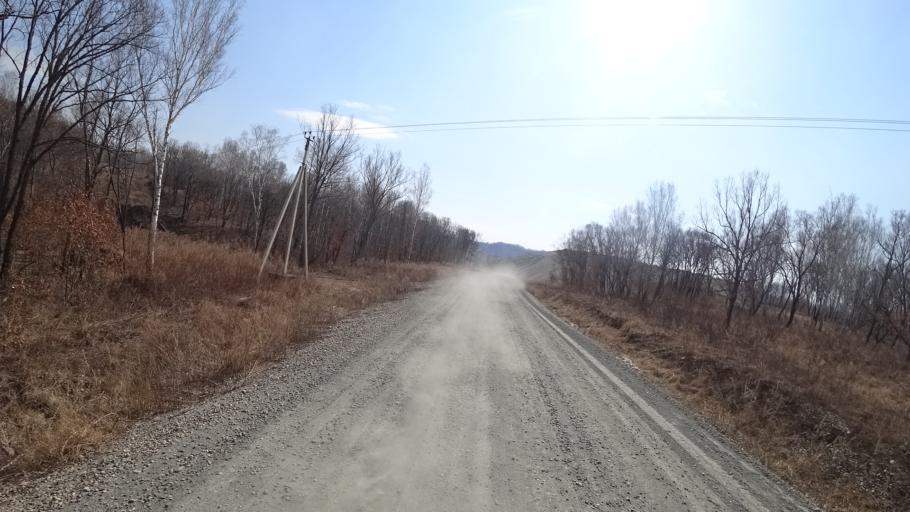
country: RU
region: Amur
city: Novobureyskiy
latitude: 49.8006
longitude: 129.9598
